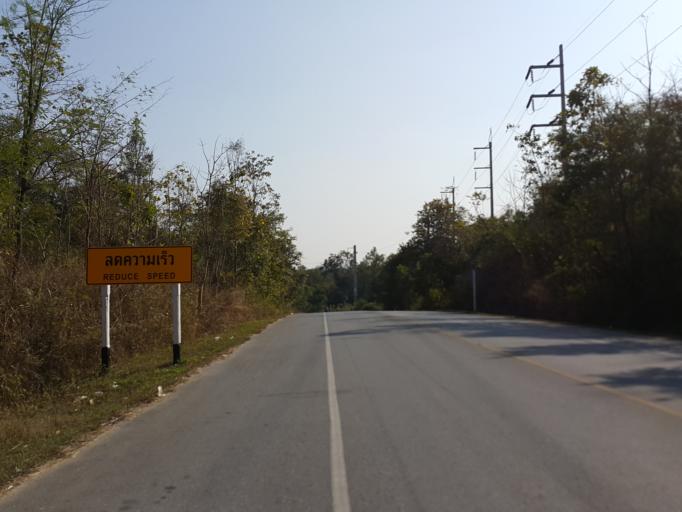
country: TH
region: Lampang
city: Chae Hom
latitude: 18.5914
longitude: 99.5483
